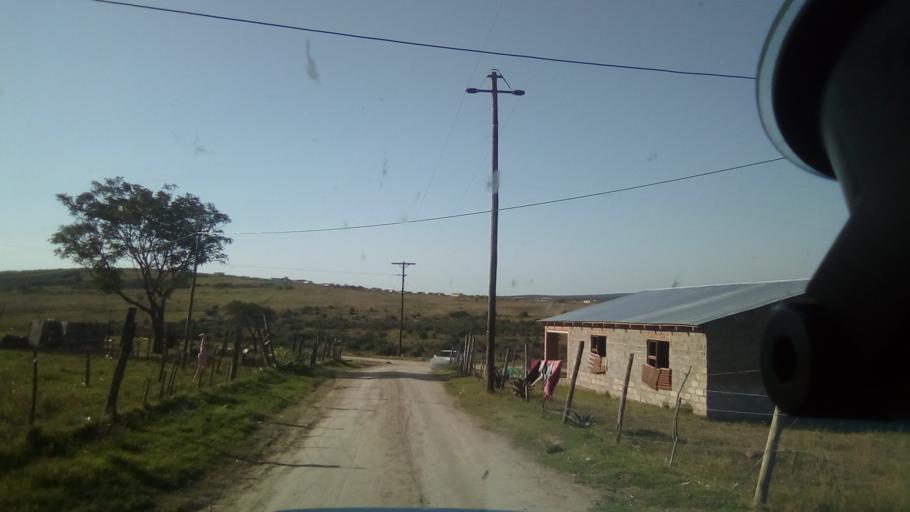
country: ZA
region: Eastern Cape
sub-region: Buffalo City Metropolitan Municipality
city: Bhisho
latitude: -32.8111
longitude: 27.3579
